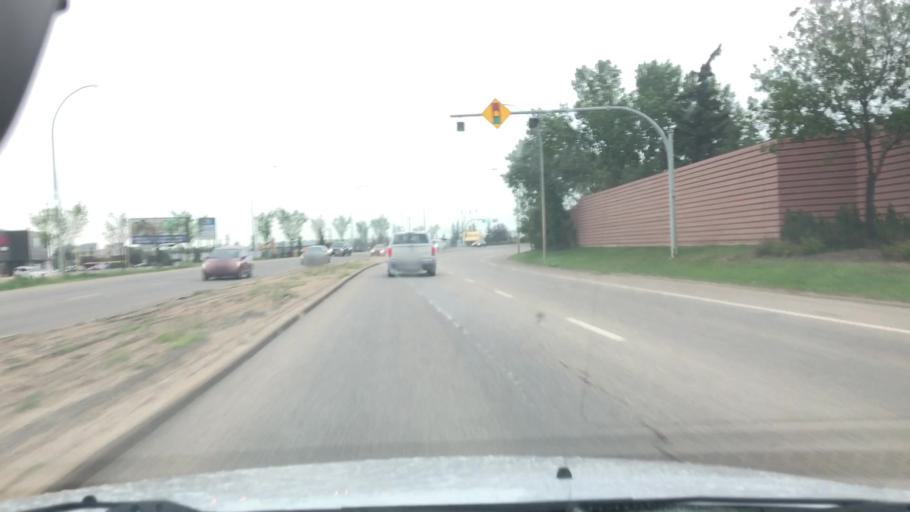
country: CA
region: Alberta
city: St. Albert
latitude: 53.5571
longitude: -113.6042
